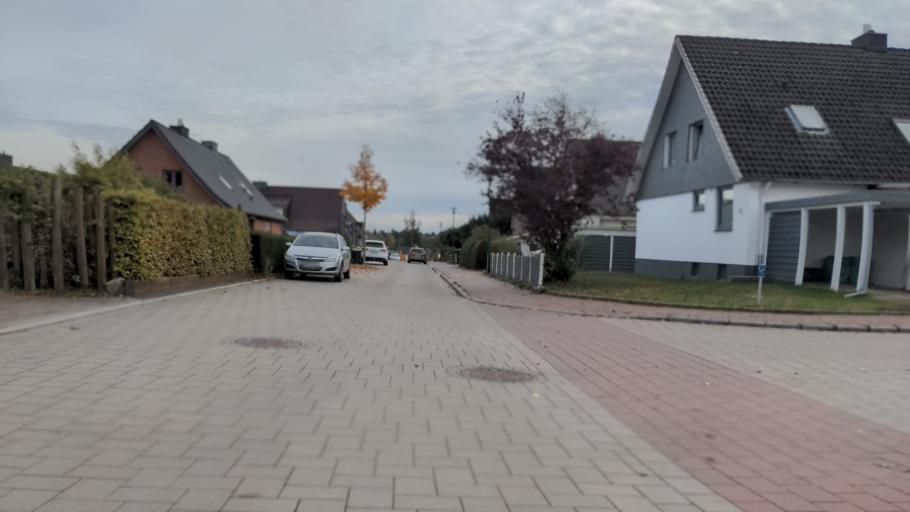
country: DE
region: Schleswig-Holstein
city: Stockelsdorf
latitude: 53.9029
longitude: 10.6588
